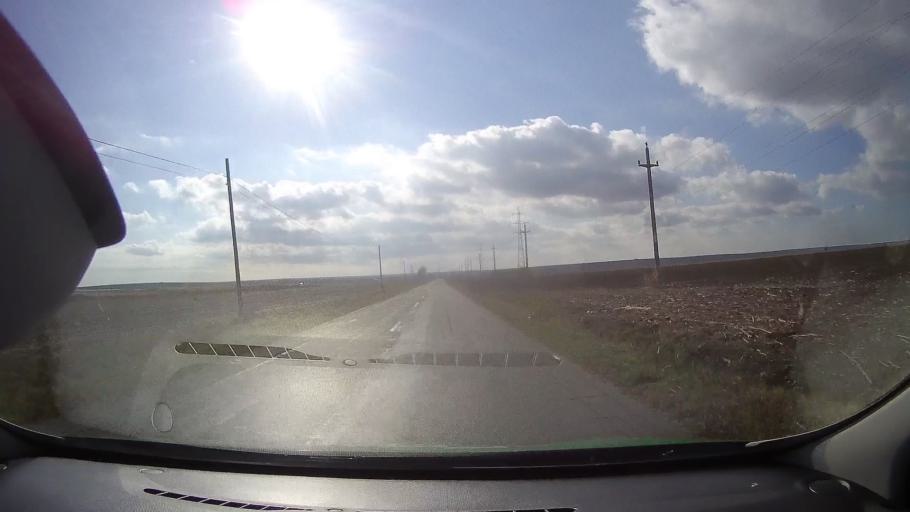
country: RO
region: Constanta
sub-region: Comuna Istria
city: Istria
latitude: 44.5393
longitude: 28.6887
